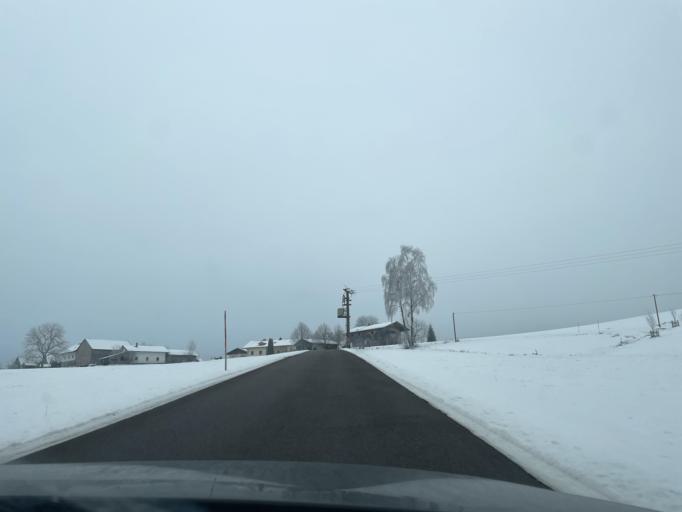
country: DE
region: Bavaria
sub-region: Lower Bavaria
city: Kollnburg
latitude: 49.0138
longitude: 12.9010
